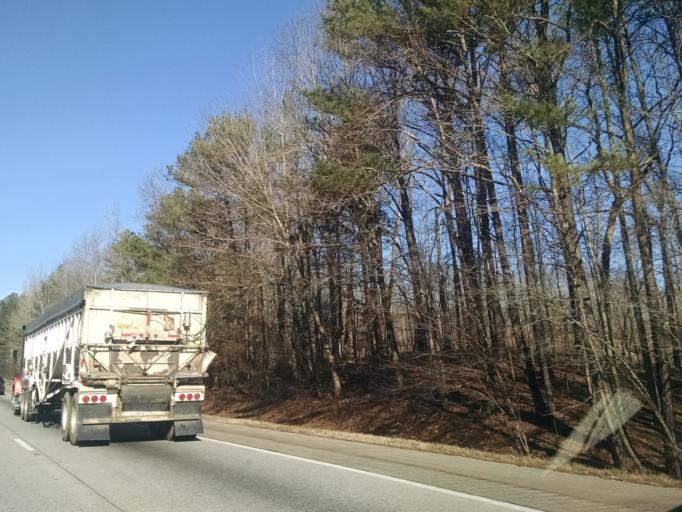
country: US
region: Georgia
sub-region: Gwinnett County
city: Sugar Hill
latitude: 34.0752
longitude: -84.0022
